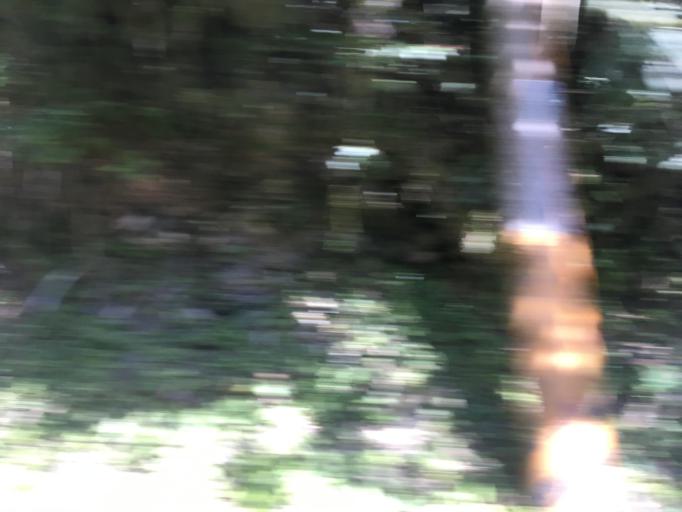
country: TW
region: Taiwan
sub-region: Yilan
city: Yilan
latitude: 24.5315
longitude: 121.5202
